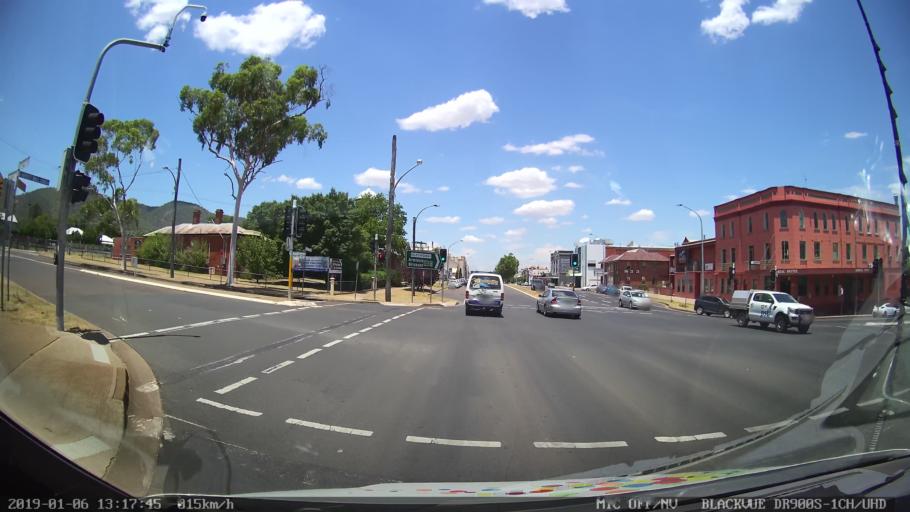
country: AU
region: New South Wales
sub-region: Tamworth Municipality
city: Tamworth
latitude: -31.0884
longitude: 150.9311
